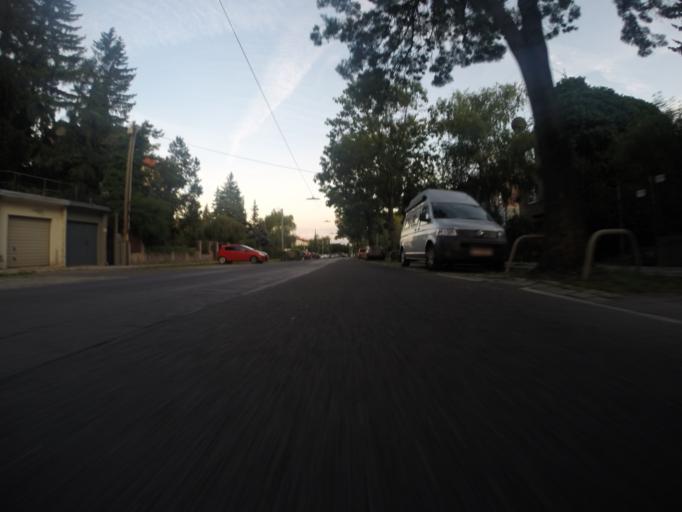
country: AT
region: Vienna
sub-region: Wien Stadt
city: Vienna
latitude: 48.2099
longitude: 16.2902
